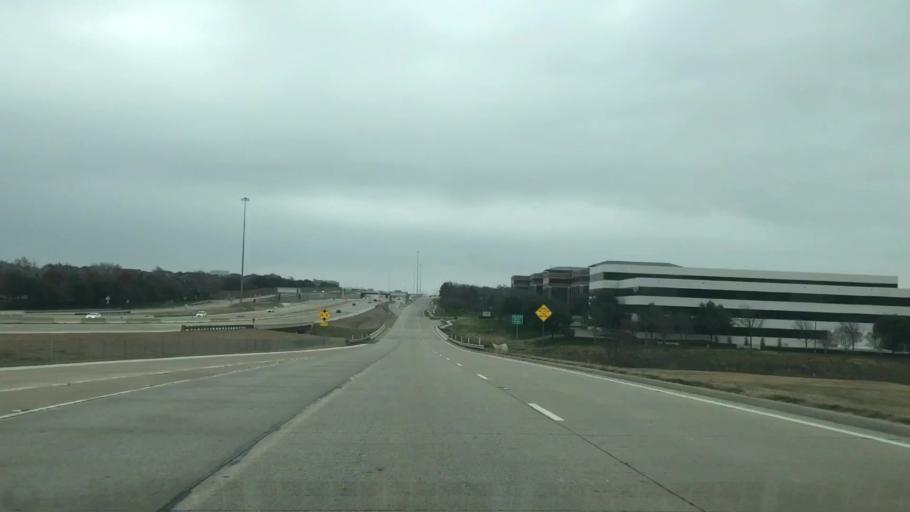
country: US
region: Texas
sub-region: Dallas County
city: Coppell
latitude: 32.8981
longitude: -96.9676
